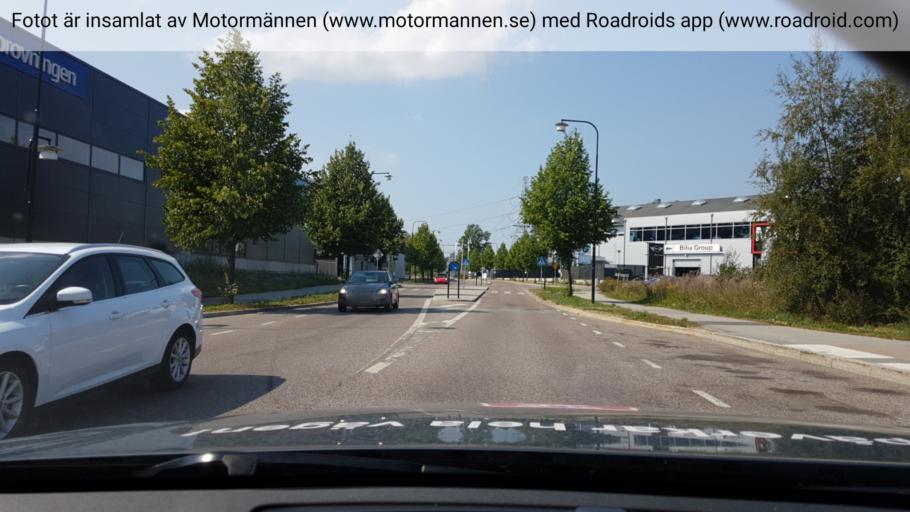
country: SE
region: Stockholm
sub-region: Huddinge Kommun
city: Segeltorp
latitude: 59.2840
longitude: 17.9413
